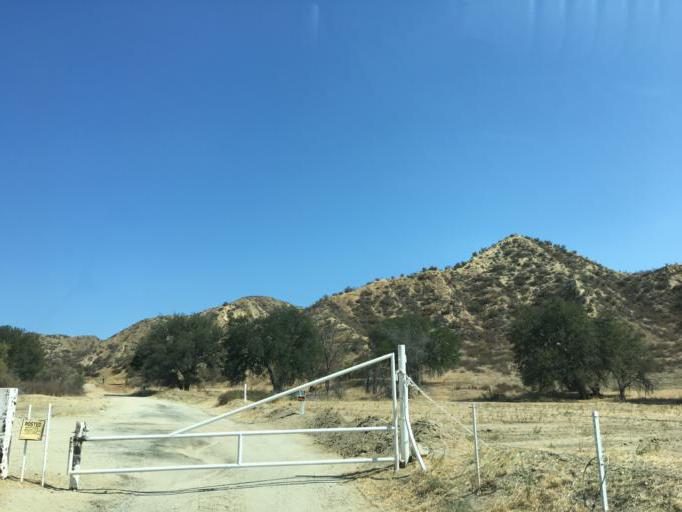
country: US
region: California
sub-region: Los Angeles County
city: Val Verde
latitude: 34.4494
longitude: -118.6726
